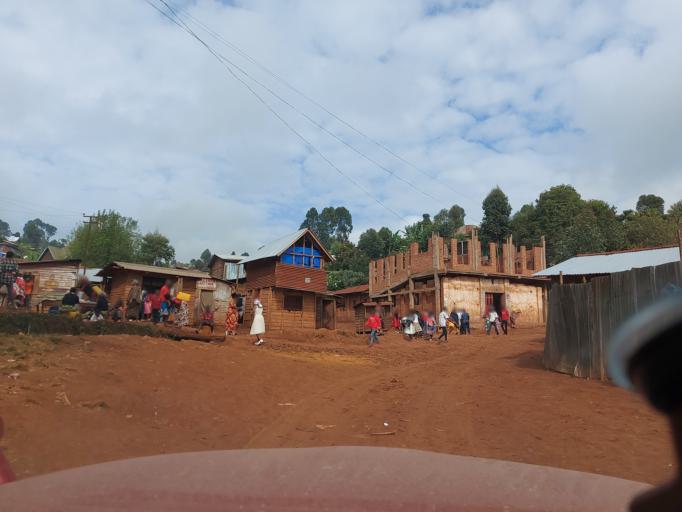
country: CD
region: South Kivu
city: Bukavu
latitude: -2.5145
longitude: 28.8390
